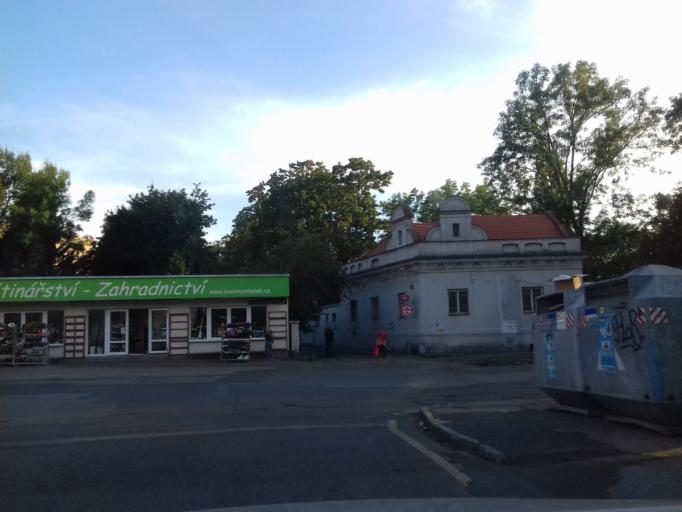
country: CZ
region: Praha
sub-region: Praha 4
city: Hodkovicky
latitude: 50.0464
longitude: 14.4406
